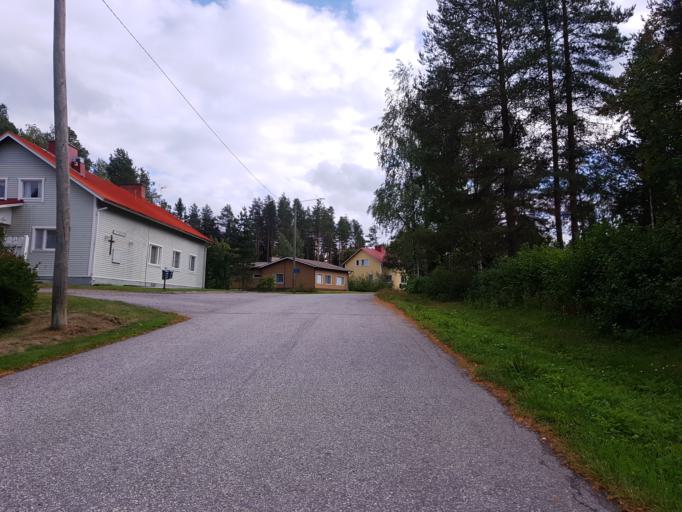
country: FI
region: Kainuu
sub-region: Kehys-Kainuu
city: Kuhmo
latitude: 64.1315
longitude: 29.5292
